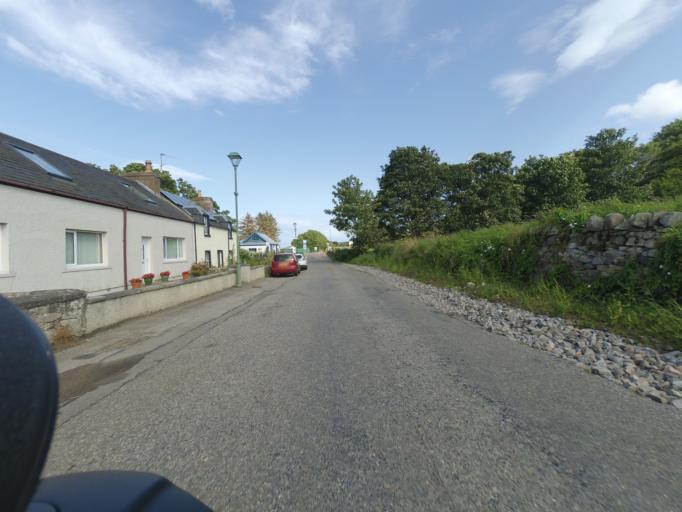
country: GB
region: Scotland
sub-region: Highland
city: Invergordon
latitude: 57.6583
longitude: -4.1457
